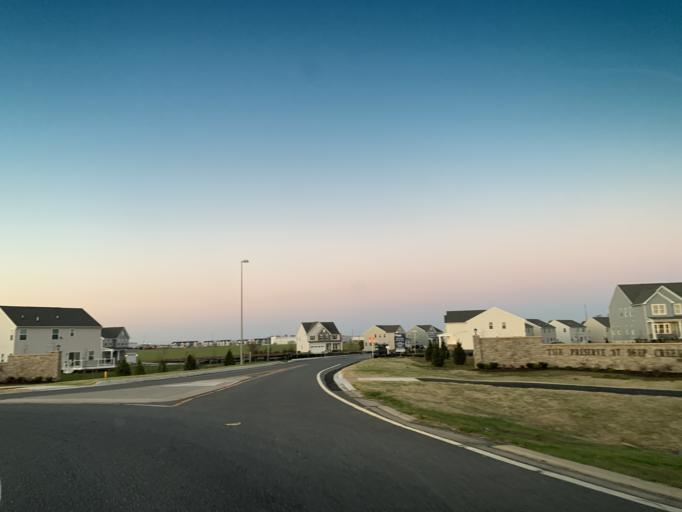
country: US
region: Delaware
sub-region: New Castle County
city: Middletown
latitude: 39.4284
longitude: -75.7386
